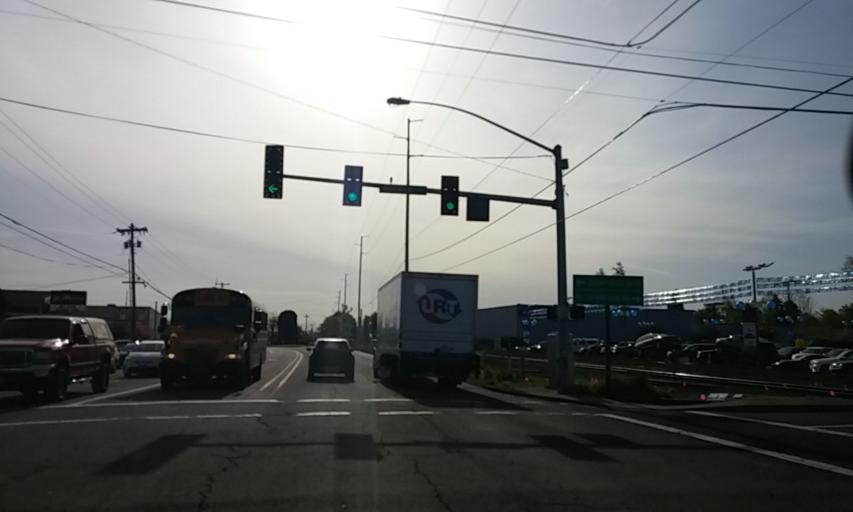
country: US
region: Oregon
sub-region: Washington County
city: Beaverton
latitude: 45.4884
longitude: -122.8149
